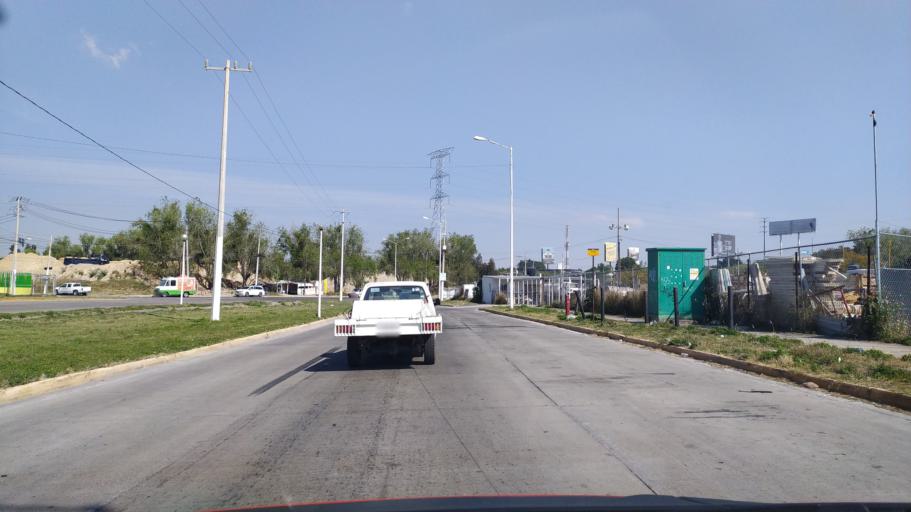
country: MX
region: Jalisco
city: Nuevo Mexico
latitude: 20.7060
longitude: -103.4594
